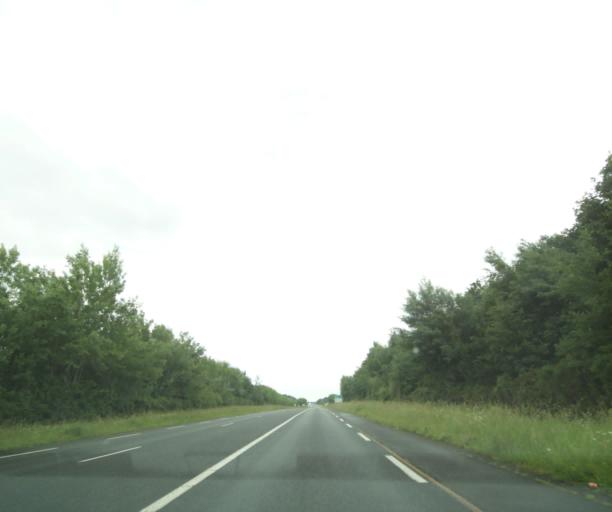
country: FR
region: Poitou-Charentes
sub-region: Departement des Deux-Sevres
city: Airvault
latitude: 46.7946
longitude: -0.2136
